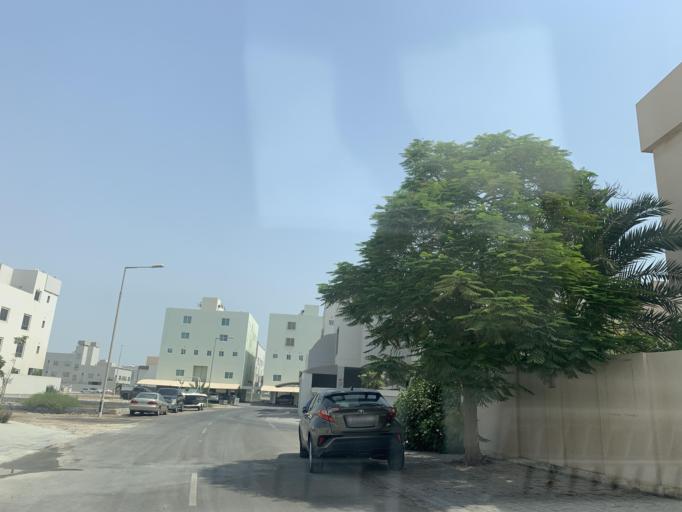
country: BH
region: Manama
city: Jidd Hafs
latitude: 26.2068
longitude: 50.5036
